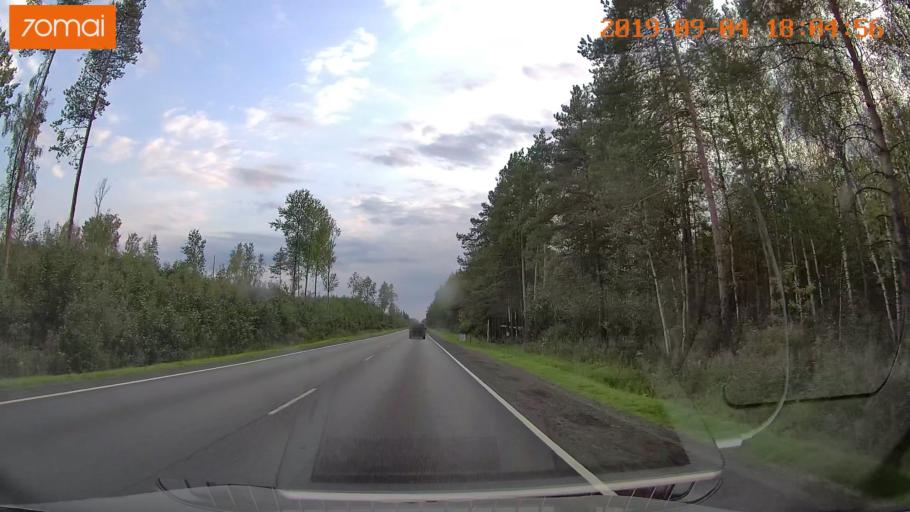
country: RU
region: Moskovskaya
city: Il'inskiy Pogost
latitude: 55.4467
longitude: 38.8327
